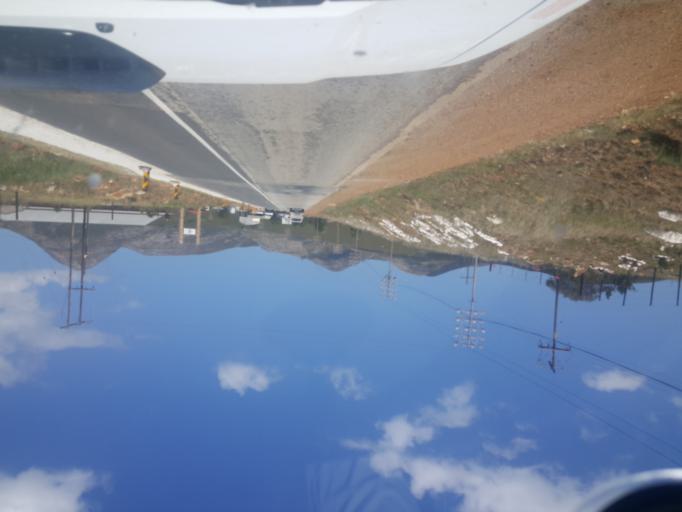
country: ZA
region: Eastern Cape
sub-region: Cacadu District Municipality
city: Kareedouw
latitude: -33.9504
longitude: 24.3014
